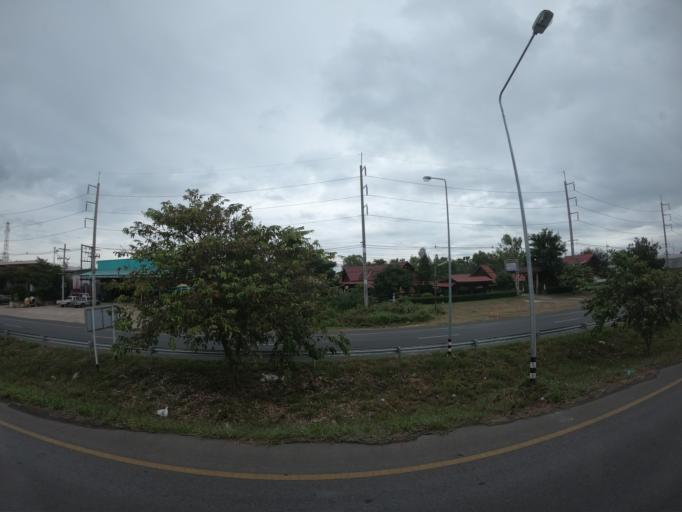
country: TH
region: Roi Et
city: Roi Et
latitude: 16.0458
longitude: 103.6243
